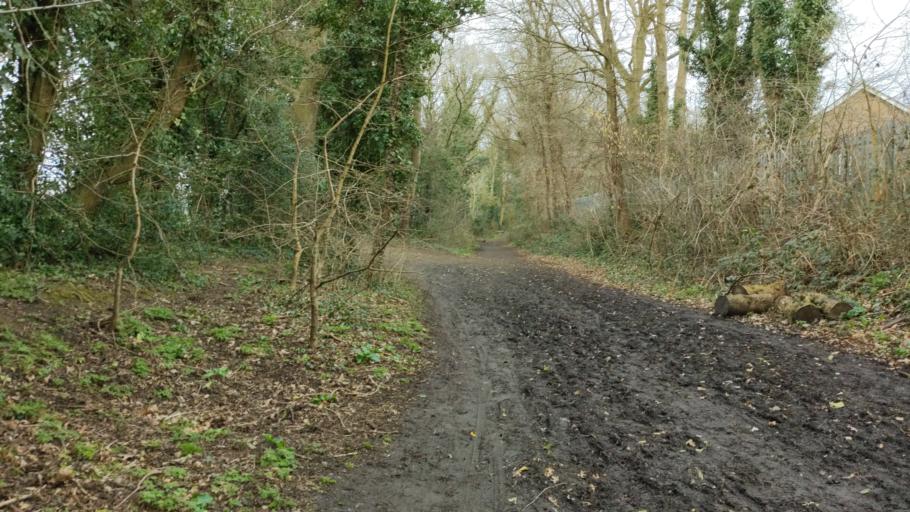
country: GB
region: England
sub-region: Hertfordshire
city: Hemel Hempstead
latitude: 51.7668
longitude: -0.4539
